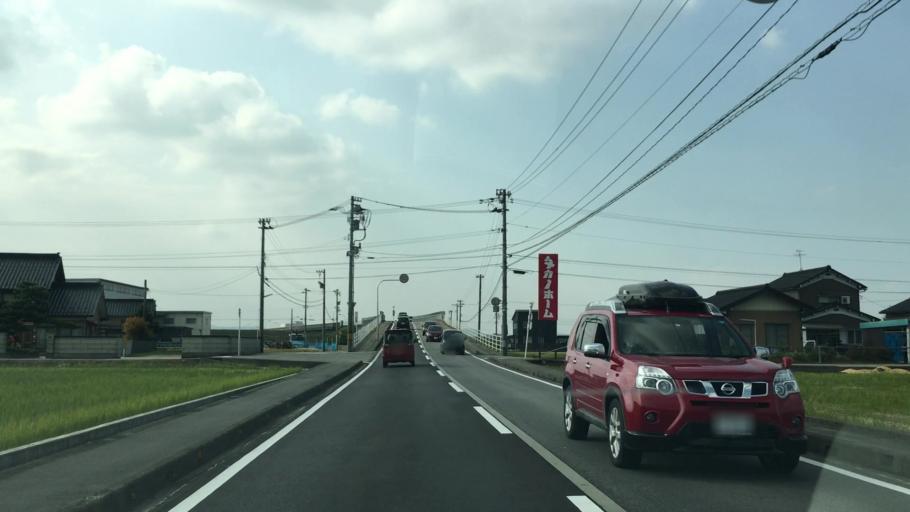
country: JP
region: Toyama
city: Toyama-shi
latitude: 36.6325
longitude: 137.1908
